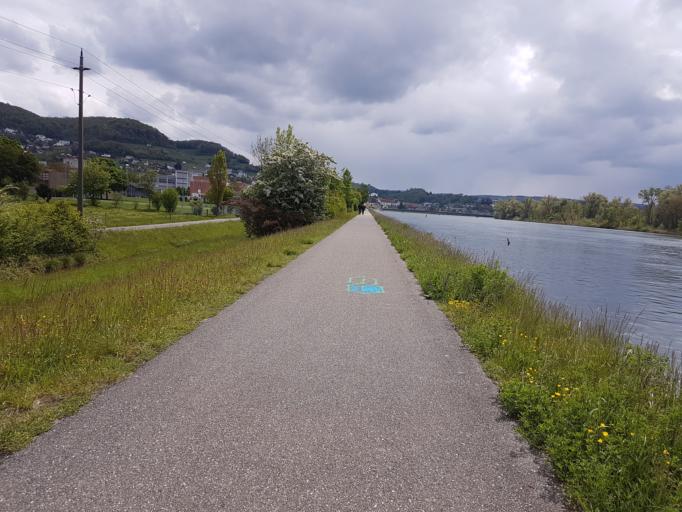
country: CH
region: Aargau
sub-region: Bezirk Zurzach
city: Klingnau
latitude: 47.5790
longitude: 8.2464
